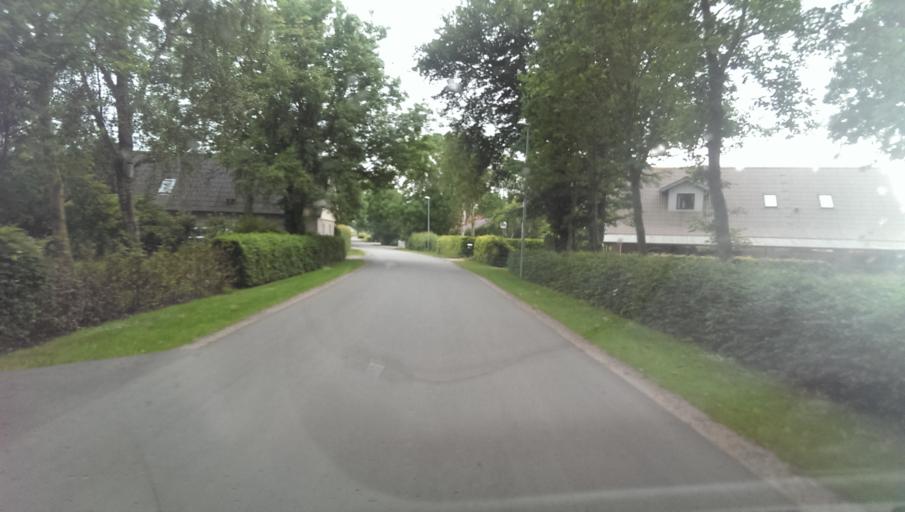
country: DK
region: South Denmark
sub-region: Esbjerg Kommune
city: Bramming
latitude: 55.4318
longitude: 8.7160
